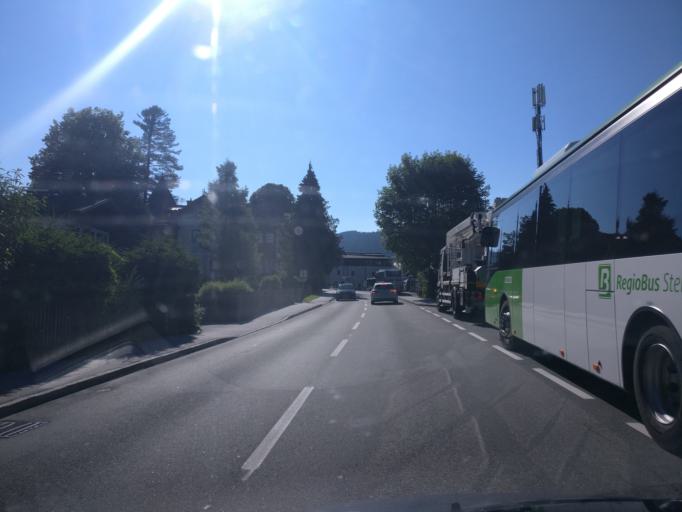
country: AT
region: Salzburg
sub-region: Politischer Bezirk Sankt Johann im Pongau
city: Radstadt
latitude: 47.3848
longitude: 13.4592
